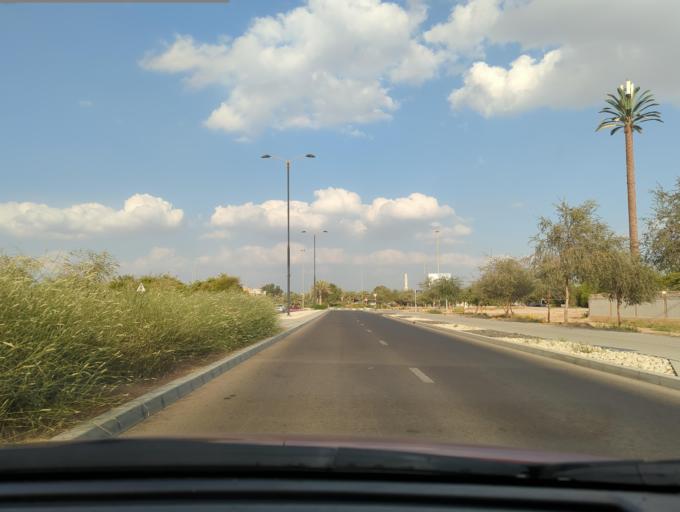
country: AE
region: Abu Dhabi
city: Al Ain
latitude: 24.1609
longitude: 55.6692
